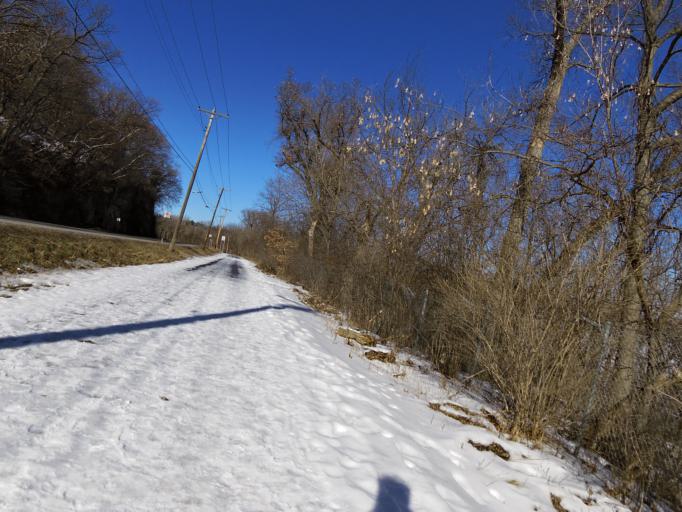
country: US
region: Minnesota
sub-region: Washington County
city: Stillwater
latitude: 45.0695
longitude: -92.8062
